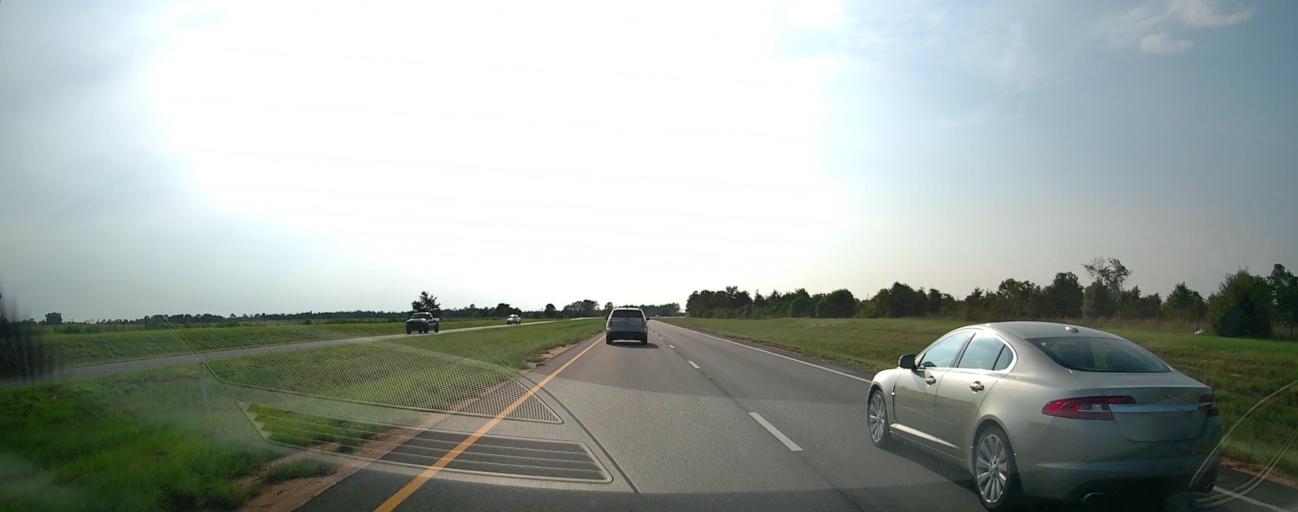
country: US
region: Georgia
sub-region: Taylor County
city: Butler
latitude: 32.5482
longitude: -84.2545
